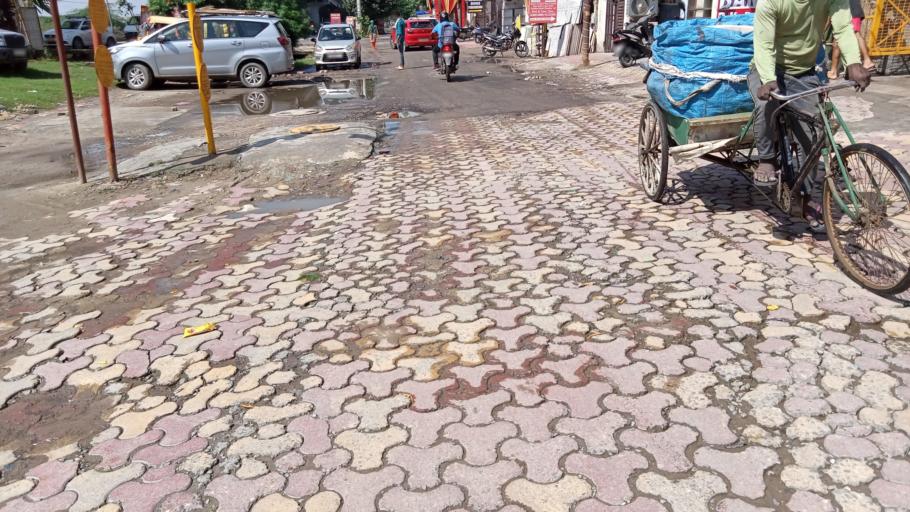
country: IN
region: Uttar Pradesh
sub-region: Ghaziabad
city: Ghaziabad
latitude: 28.6578
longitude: 77.3762
